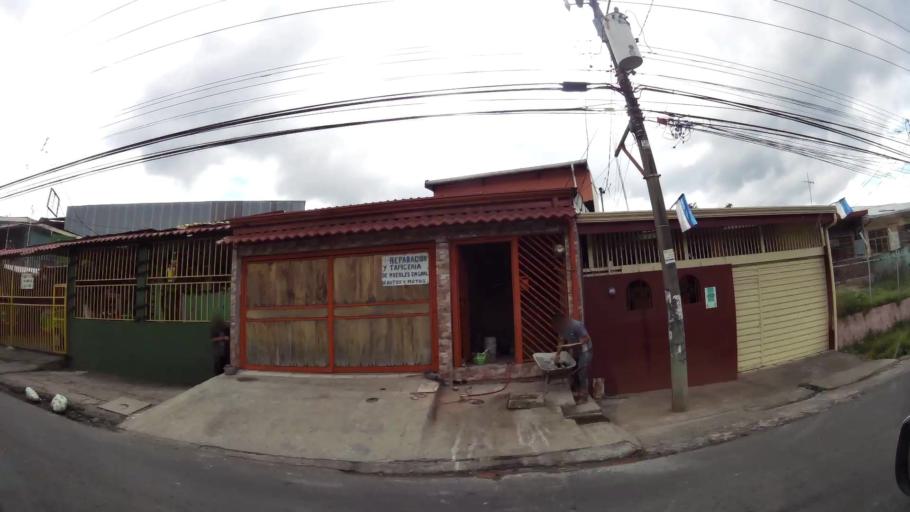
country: CR
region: San Jose
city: Alajuelita
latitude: 9.8986
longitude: -84.0933
